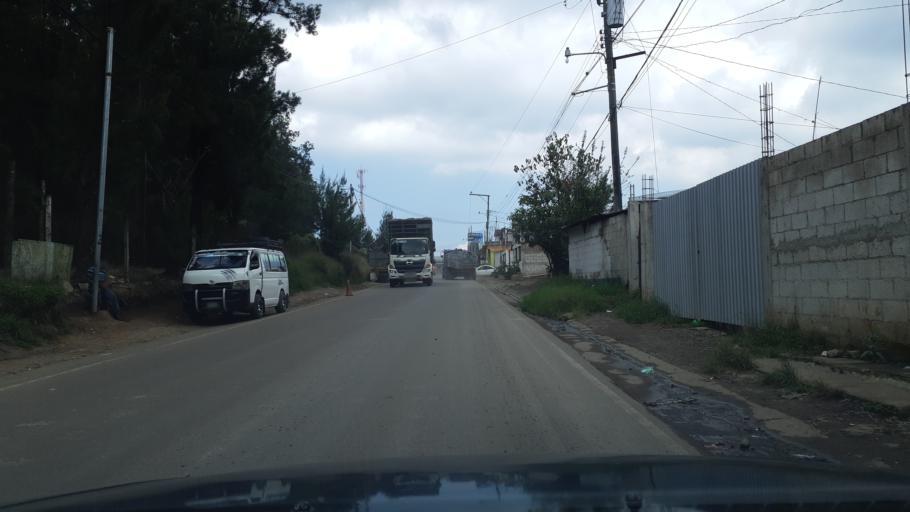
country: GT
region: Chimaltenango
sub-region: Municipio de Chimaltenango
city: Chimaltenango
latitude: 14.6853
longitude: -90.7962
